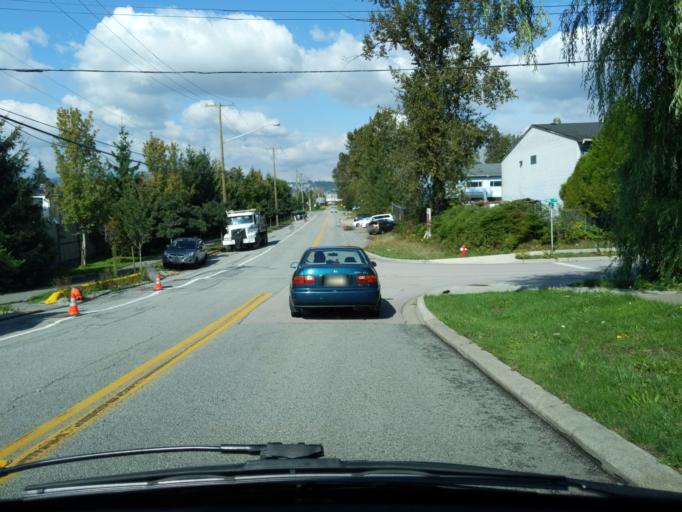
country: CA
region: British Columbia
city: New Westminster
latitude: 49.2096
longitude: -122.8563
